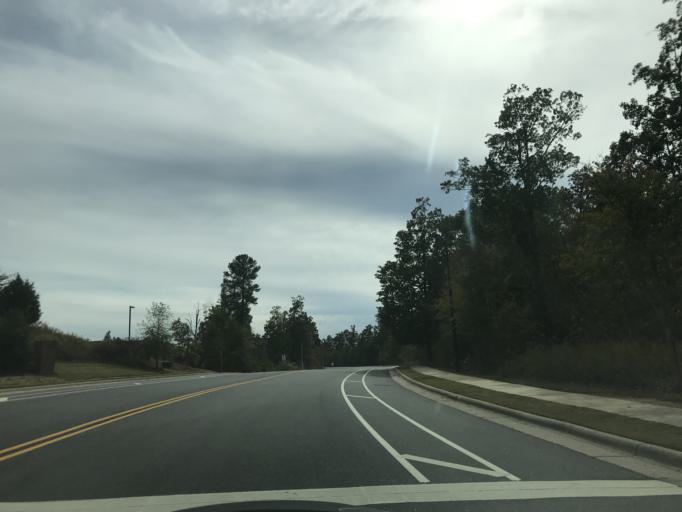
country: US
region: North Carolina
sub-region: Wake County
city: Wake Forest
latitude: 35.9559
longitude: -78.5448
